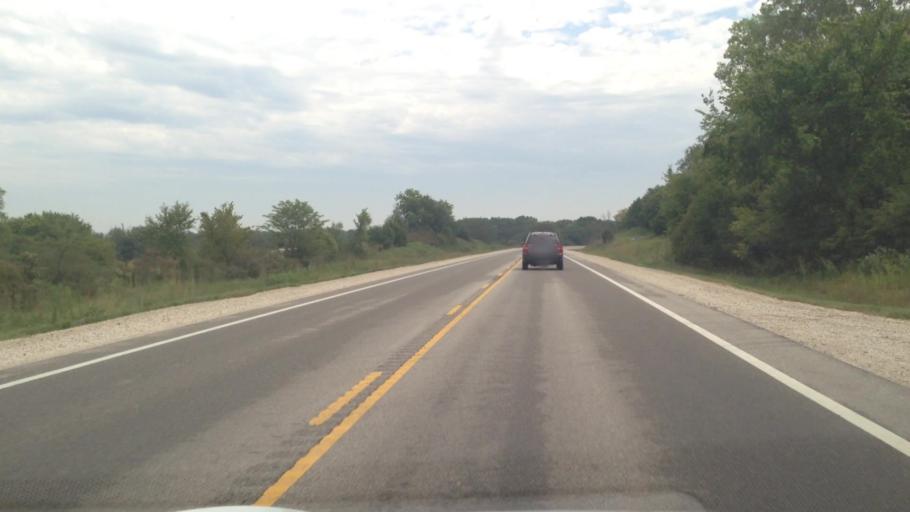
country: US
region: Kansas
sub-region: Allen County
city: Iola
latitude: 37.9145
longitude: -95.1436
